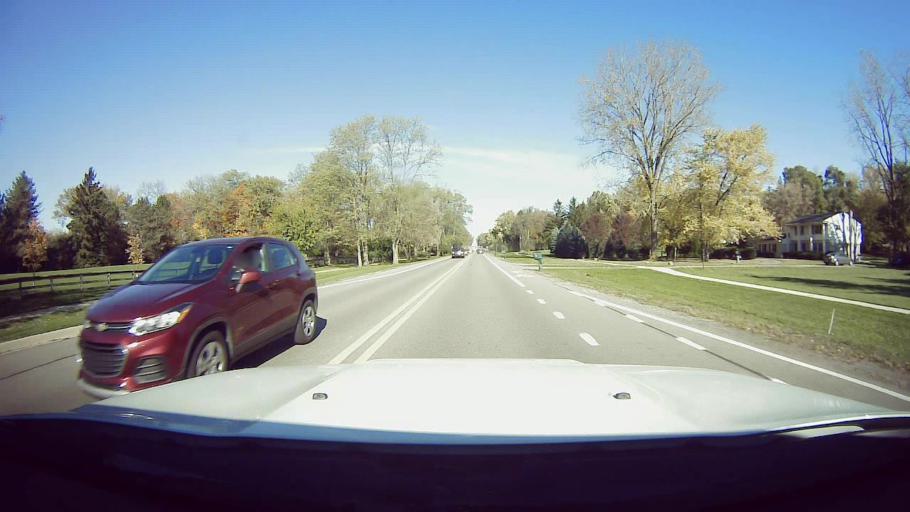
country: US
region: Michigan
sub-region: Oakland County
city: Farmington Hills
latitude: 42.4793
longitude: -83.3772
